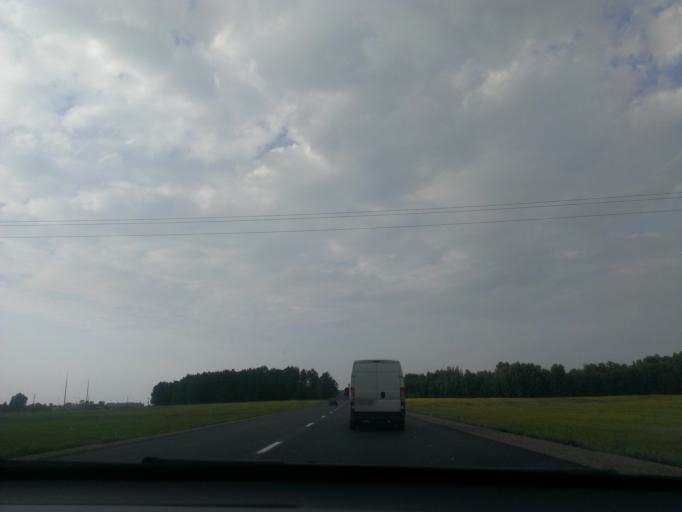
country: LV
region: Lecava
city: Iecava
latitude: 56.6487
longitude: 24.2289
